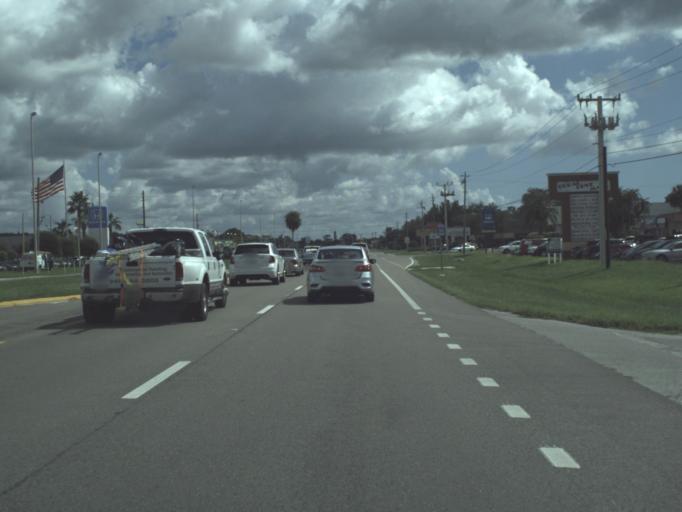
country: US
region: Florida
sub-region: Sarasota County
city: Gulf Gate Estates
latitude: 27.2491
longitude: -82.5132
